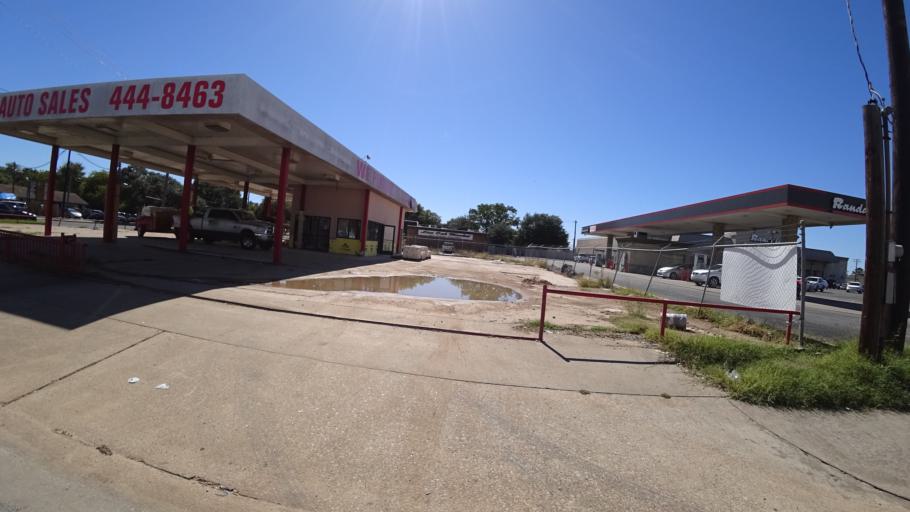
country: US
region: Texas
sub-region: Travis County
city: Rollingwood
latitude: 30.2297
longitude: -97.7890
